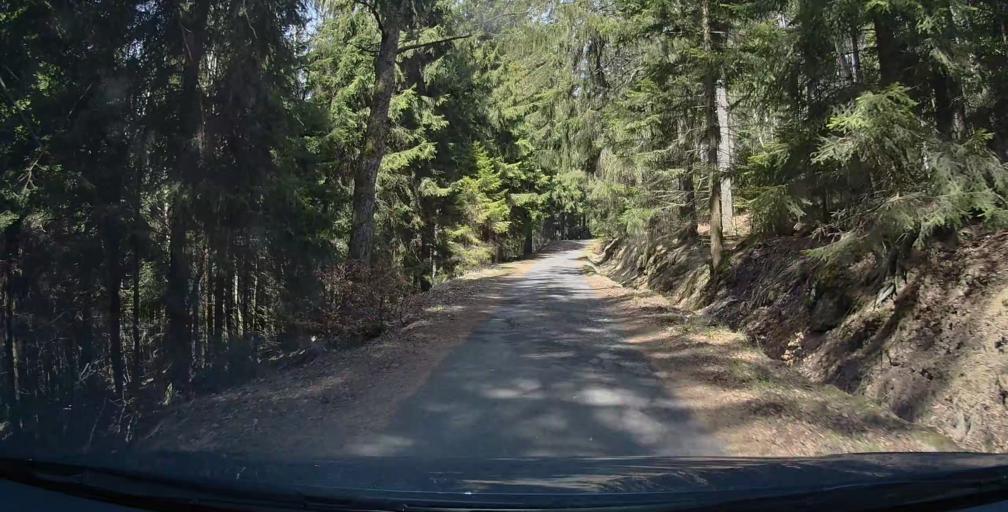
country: CZ
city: Machov
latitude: 50.4705
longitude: 16.2893
